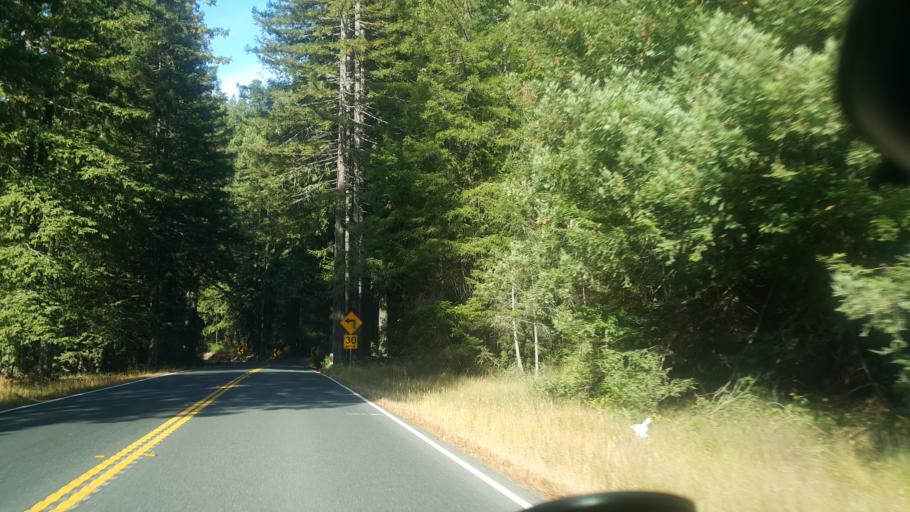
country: US
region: California
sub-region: Mendocino County
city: Brooktrails
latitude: 39.3527
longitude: -123.5591
